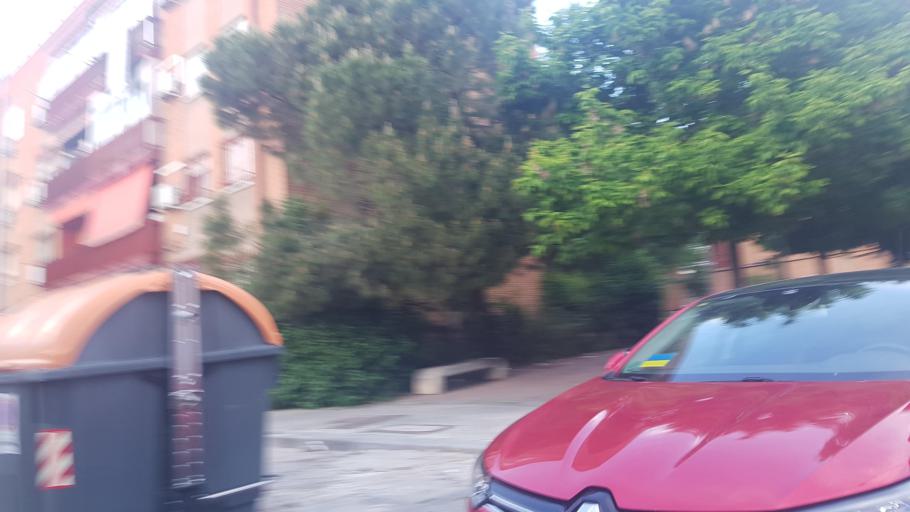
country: ES
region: Madrid
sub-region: Provincia de Madrid
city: Puente de Vallecas
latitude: 40.3719
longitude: -3.6579
